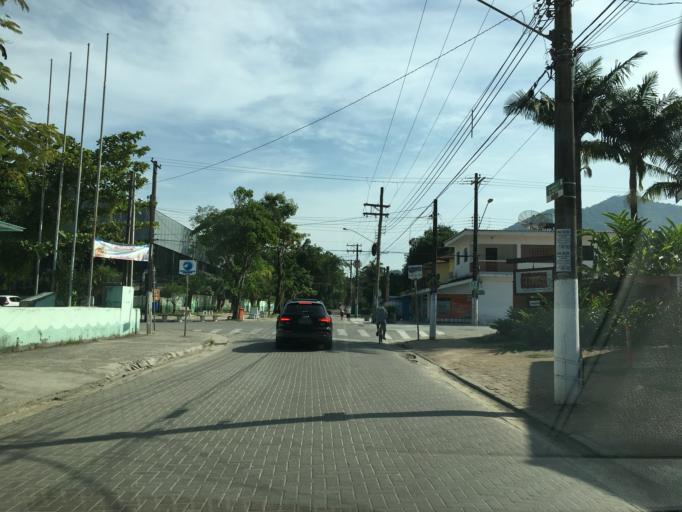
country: BR
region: Sao Paulo
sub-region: Sao Sebastiao
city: Sao Sebastiao
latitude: -23.7661
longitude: -45.7282
